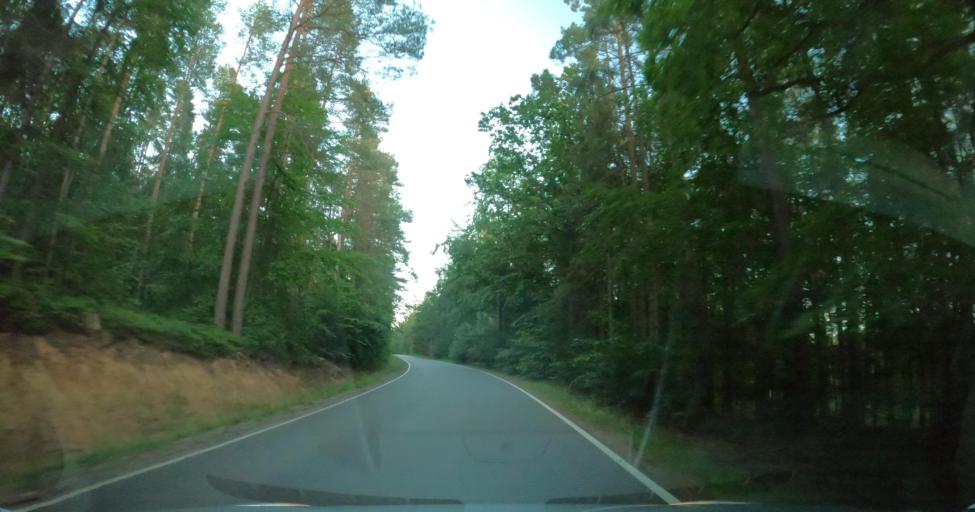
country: PL
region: Pomeranian Voivodeship
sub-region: Powiat leborski
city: Lebork
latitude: 54.5051
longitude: 17.8179
